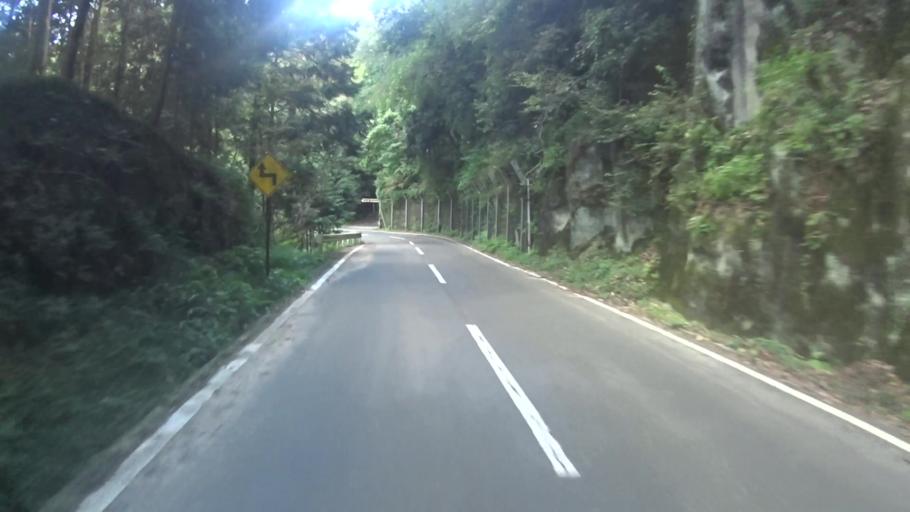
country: JP
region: Mie
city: Nabari
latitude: 34.7180
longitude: 136.0021
